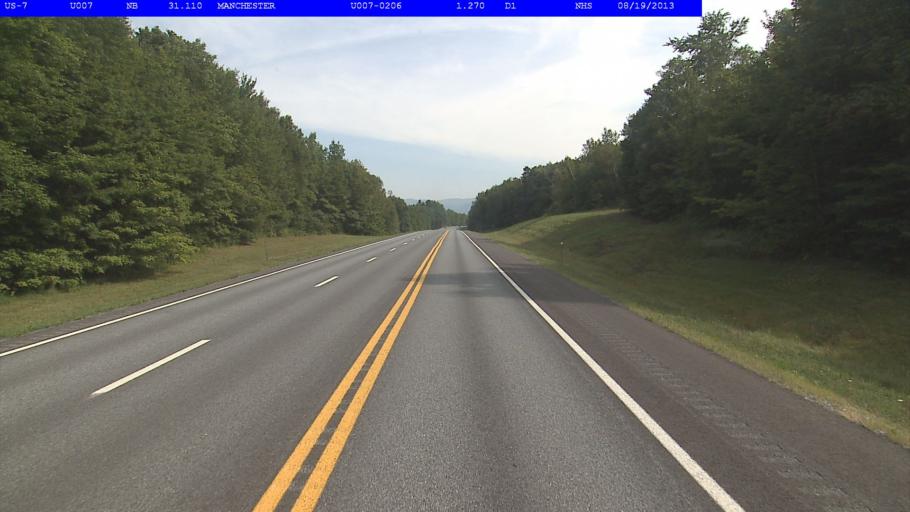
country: US
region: Vermont
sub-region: Bennington County
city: Manchester Center
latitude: 43.1319
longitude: -73.0644
